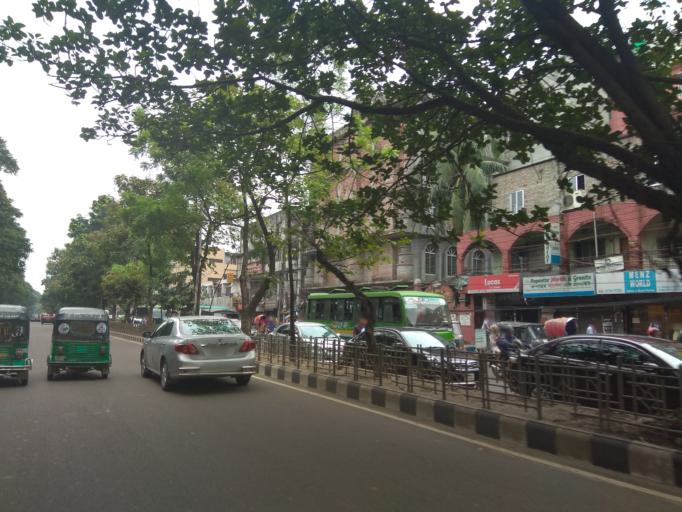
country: BD
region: Dhaka
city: Azimpur
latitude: 23.7618
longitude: 90.3835
